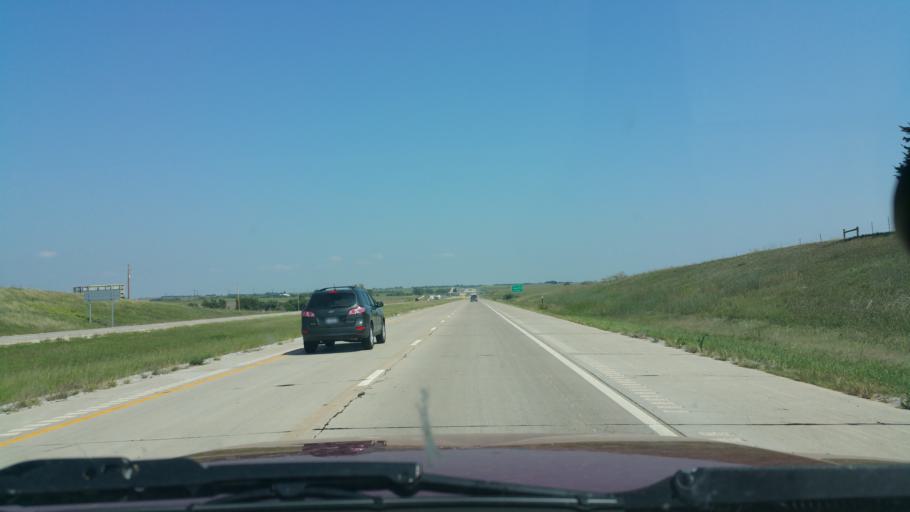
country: US
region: Kansas
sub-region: Dickinson County
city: Abilene
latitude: 38.9438
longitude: -97.1867
